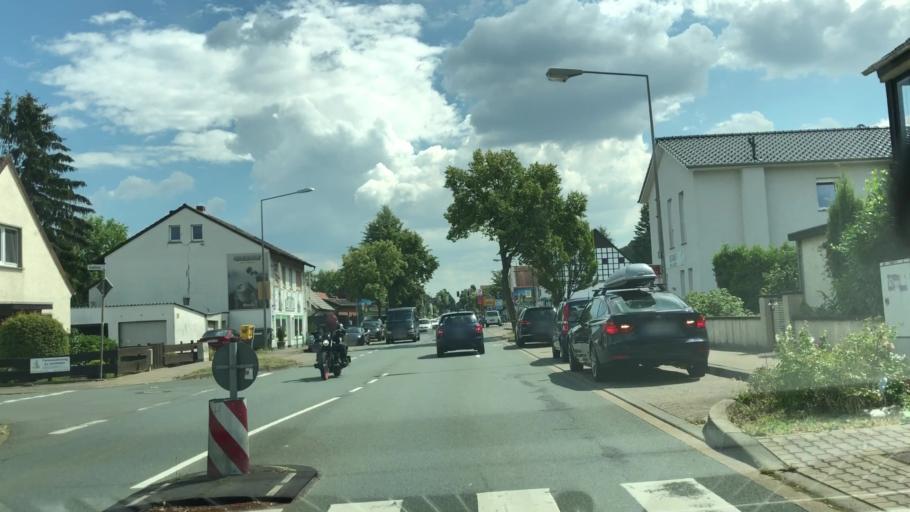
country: DE
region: North Rhine-Westphalia
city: Porta Westfalica
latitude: 52.2556
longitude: 8.9090
